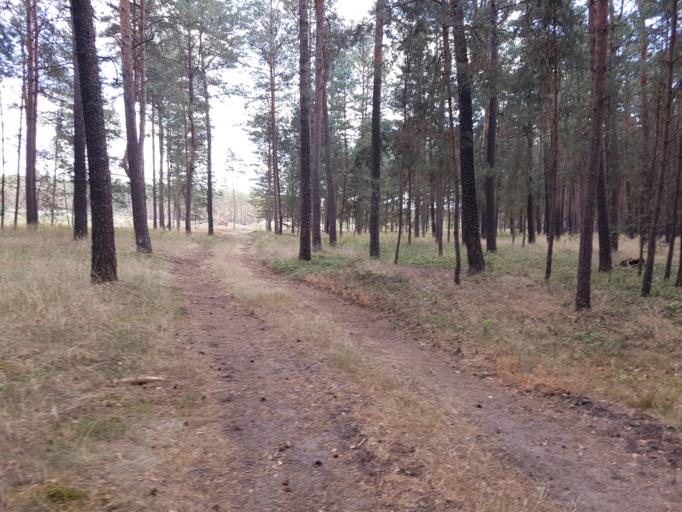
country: DE
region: Brandenburg
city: Cottbus
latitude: 51.7123
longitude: 14.4436
